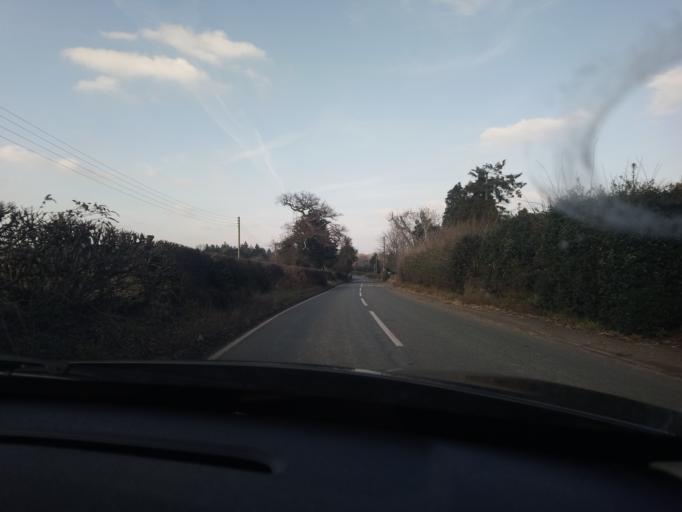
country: GB
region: England
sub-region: Shropshire
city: Bicton
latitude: 52.7407
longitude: -2.7784
